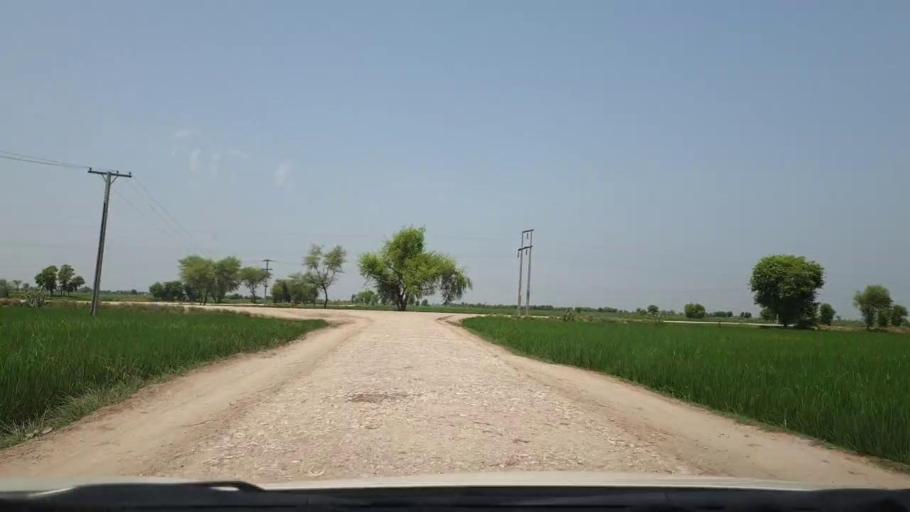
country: PK
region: Sindh
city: Radhan
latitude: 27.2498
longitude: 67.9822
